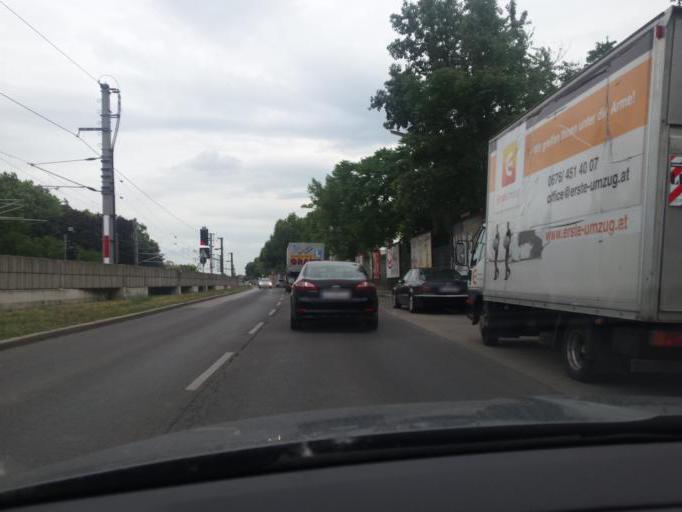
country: AT
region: Vienna
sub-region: Wien Stadt
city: Vienna
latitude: 48.1726
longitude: 16.4076
